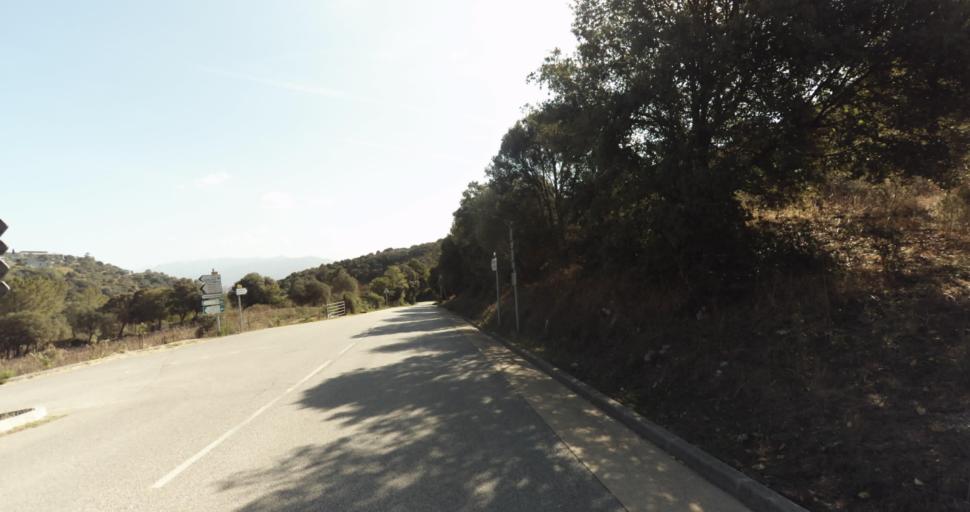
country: FR
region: Corsica
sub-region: Departement de la Corse-du-Sud
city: Ajaccio
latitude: 41.9291
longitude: 8.7035
